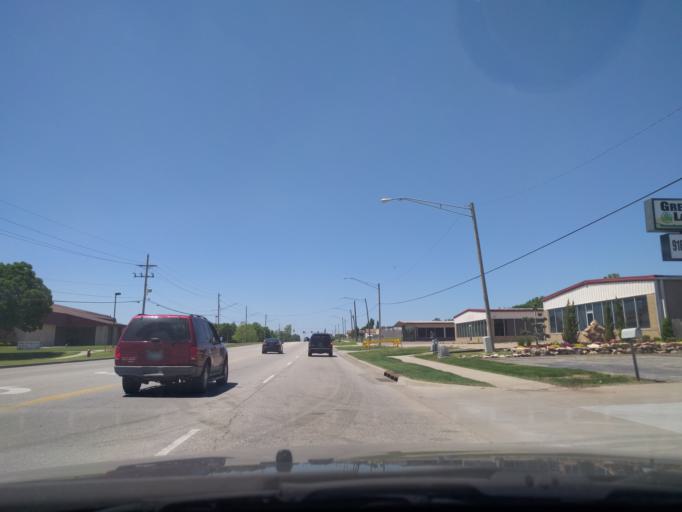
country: US
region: Oklahoma
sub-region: Tulsa County
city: Broken Arrow
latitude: 36.0610
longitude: -95.8016
